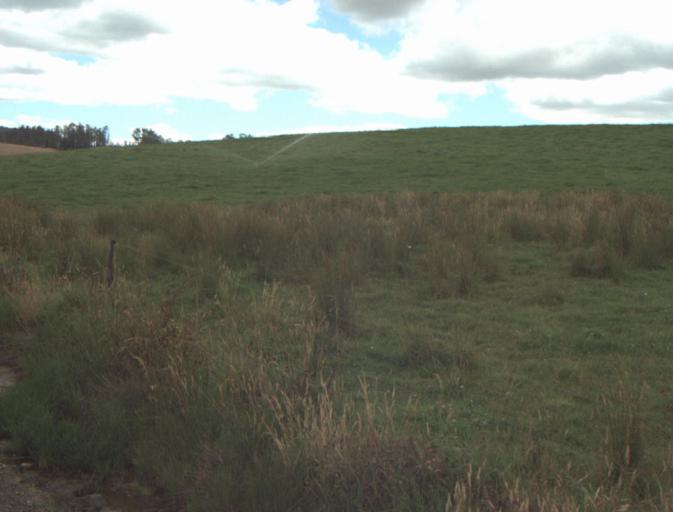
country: AU
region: Tasmania
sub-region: Launceston
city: Mayfield
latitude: -41.2387
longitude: 147.2064
